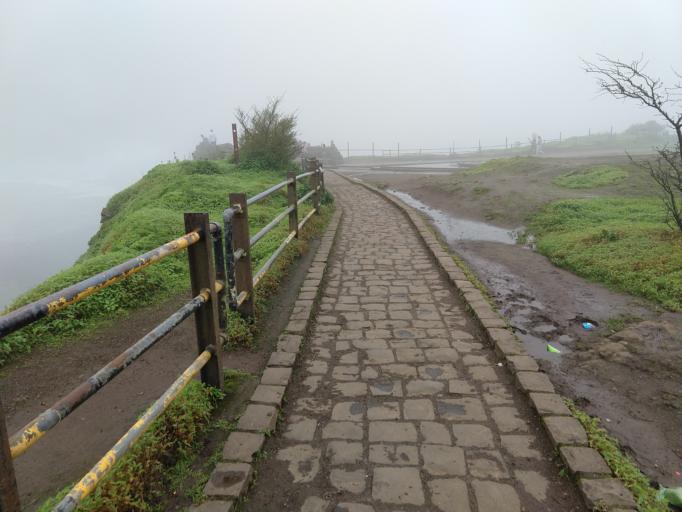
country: IN
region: Maharashtra
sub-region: Pune Division
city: Kharakvasla
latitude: 18.3665
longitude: 73.7517
